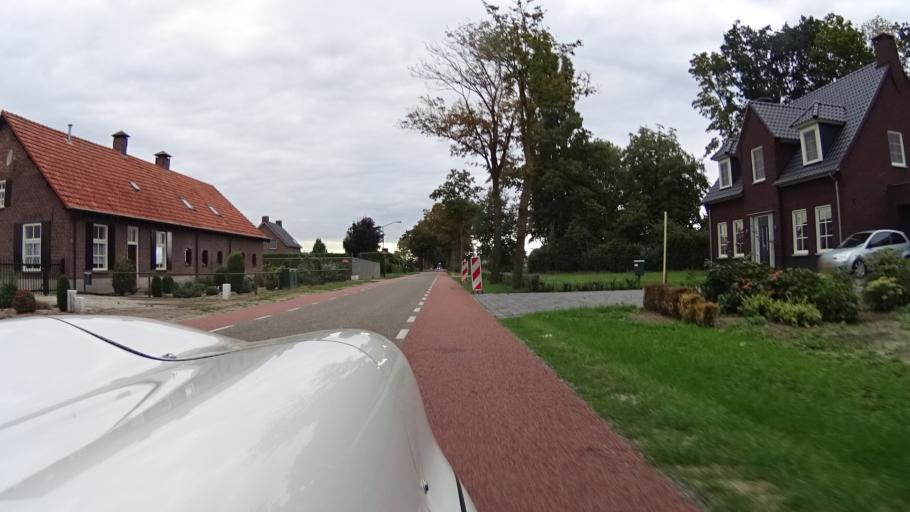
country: NL
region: North Brabant
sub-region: Gemeente Bernheze
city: Loosbroek
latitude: 51.6662
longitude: 5.5392
